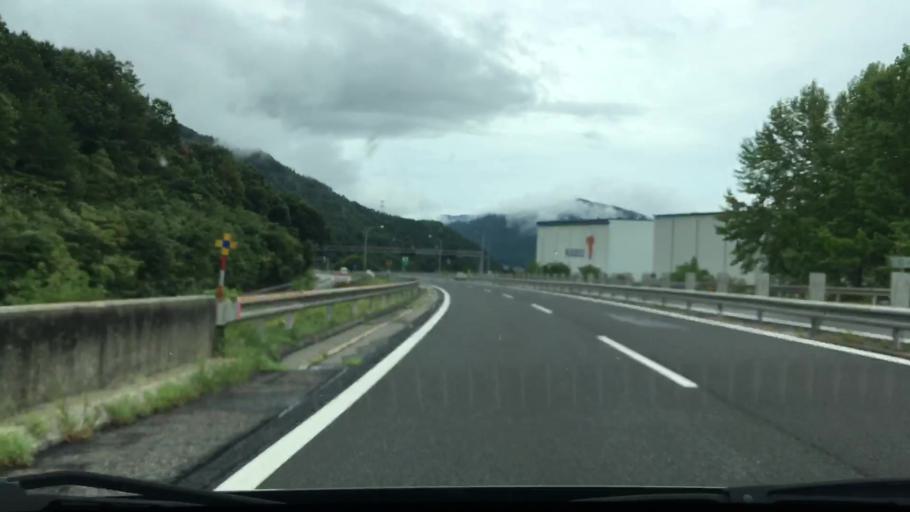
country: JP
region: Hiroshima
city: Hiroshima-shi
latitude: 34.5735
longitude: 132.4568
